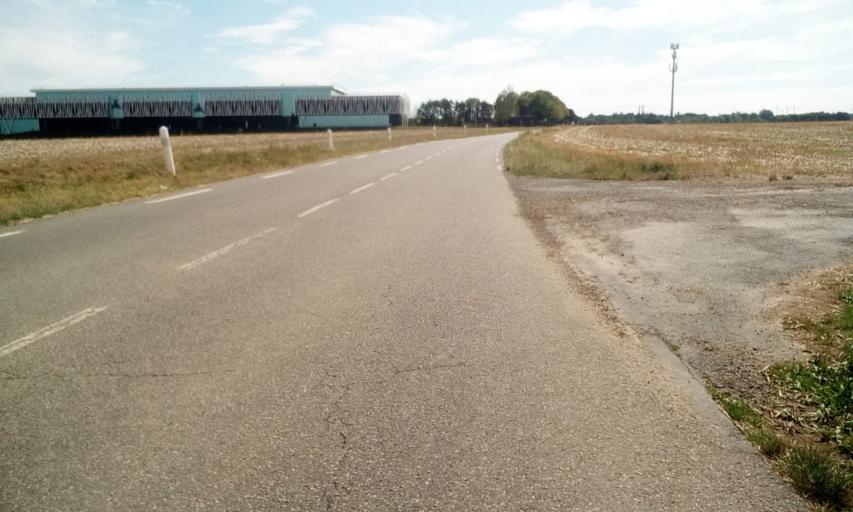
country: FR
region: Lower Normandy
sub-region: Departement du Calvados
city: Louvigny
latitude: 49.1424
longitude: -0.4059
